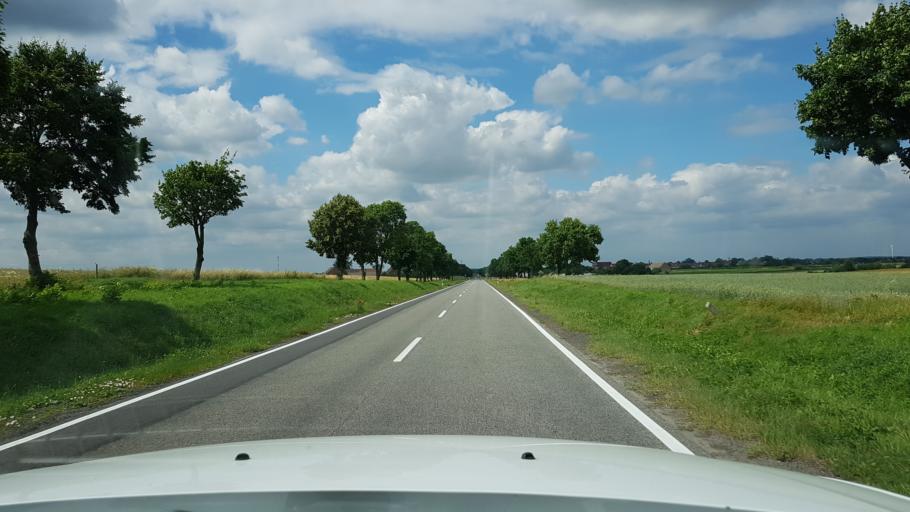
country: PL
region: West Pomeranian Voivodeship
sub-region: Powiat gryfinski
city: Mieszkowice
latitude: 52.7697
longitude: 14.4989
